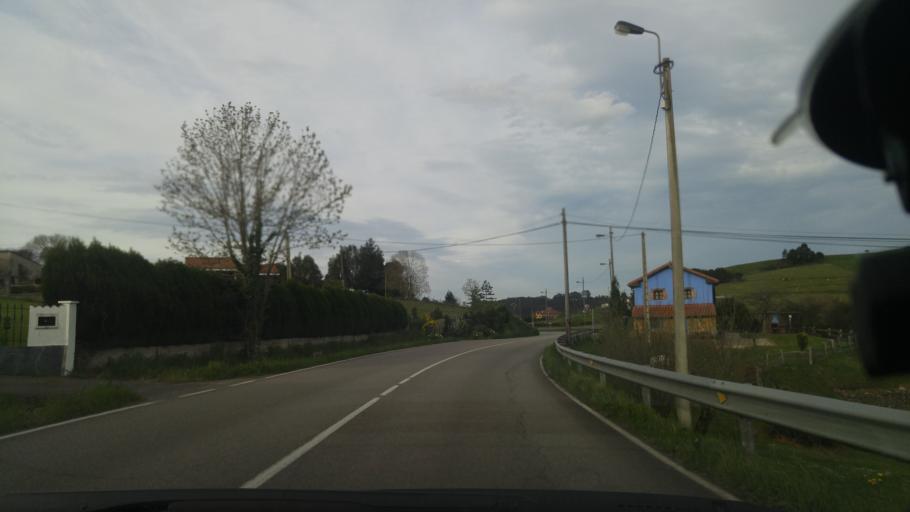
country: ES
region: Asturias
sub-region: Province of Asturias
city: Corvera de Asturias
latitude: 43.4741
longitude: -5.8458
